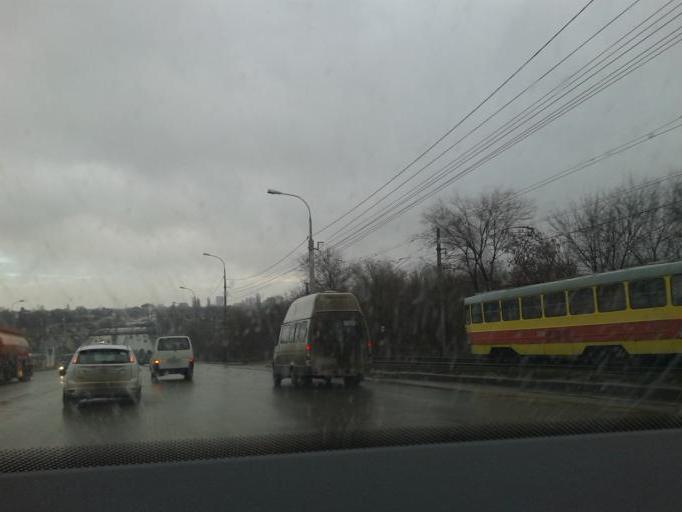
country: RU
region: Volgograd
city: Volgograd
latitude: 48.6847
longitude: 44.4512
